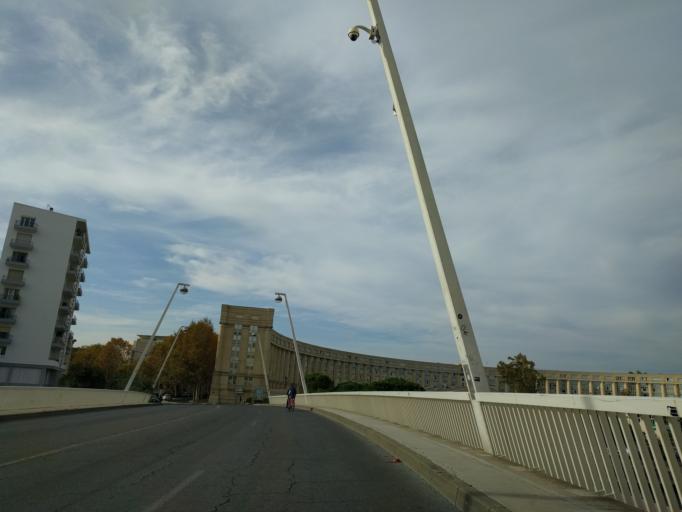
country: FR
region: Languedoc-Roussillon
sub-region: Departement de l'Herault
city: Montpellier
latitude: 43.6064
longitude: 3.8975
